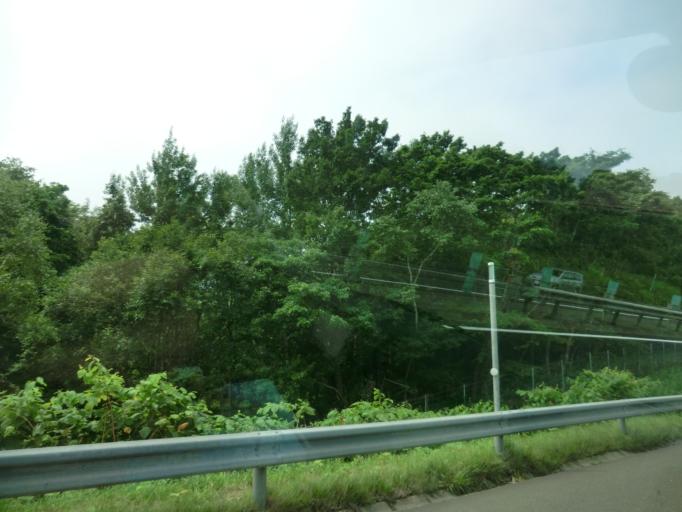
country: JP
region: Hokkaido
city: Chitose
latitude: 42.8489
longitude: 141.5744
